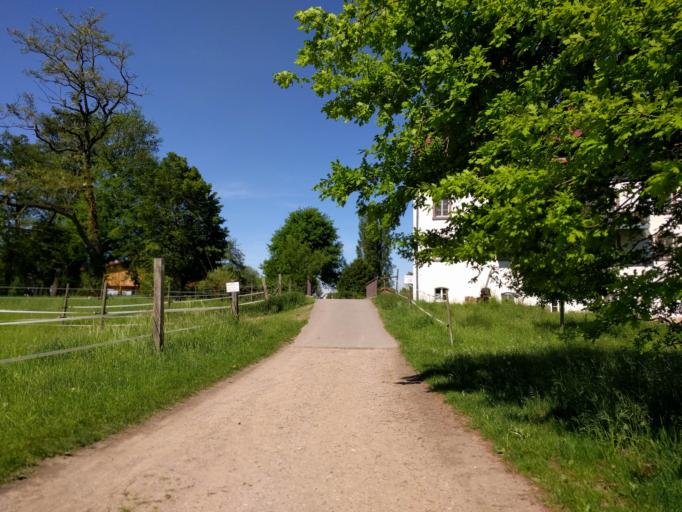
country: DE
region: Rheinland-Pfalz
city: Hassloch
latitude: 49.3496
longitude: 8.2368
